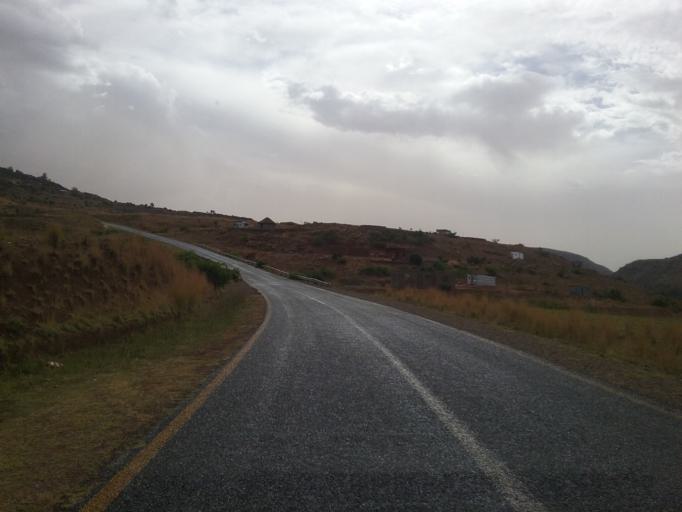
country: LS
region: Quthing
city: Quthing
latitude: -30.3668
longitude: 27.7166
